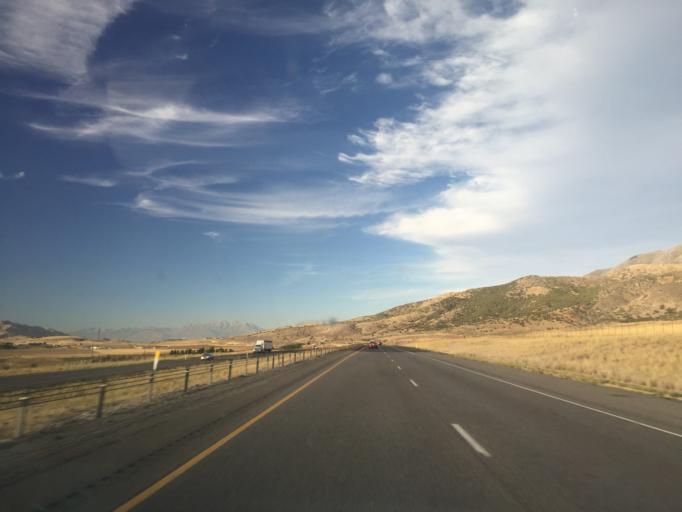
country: US
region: Utah
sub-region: Utah County
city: Santaquin
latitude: 39.9070
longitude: -111.8230
